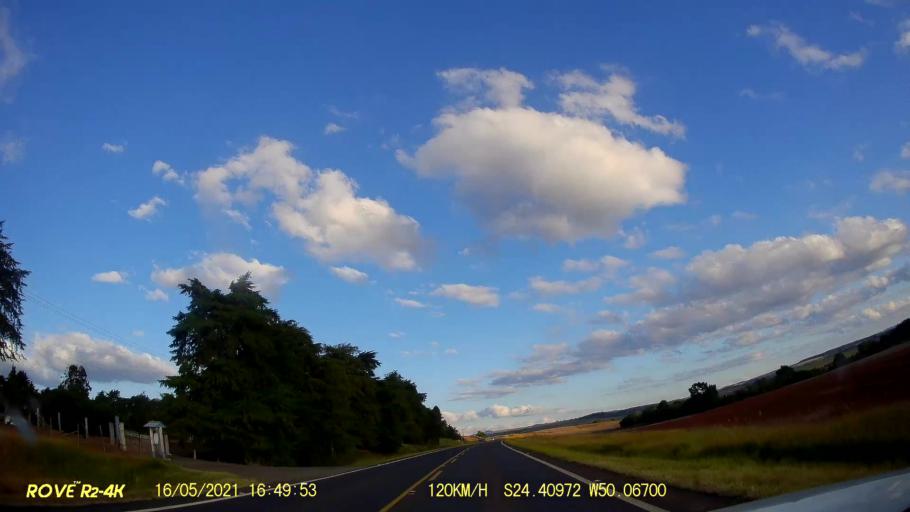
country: BR
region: Parana
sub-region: Pirai Do Sul
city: Pirai do Sul
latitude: -24.4100
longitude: -50.0668
